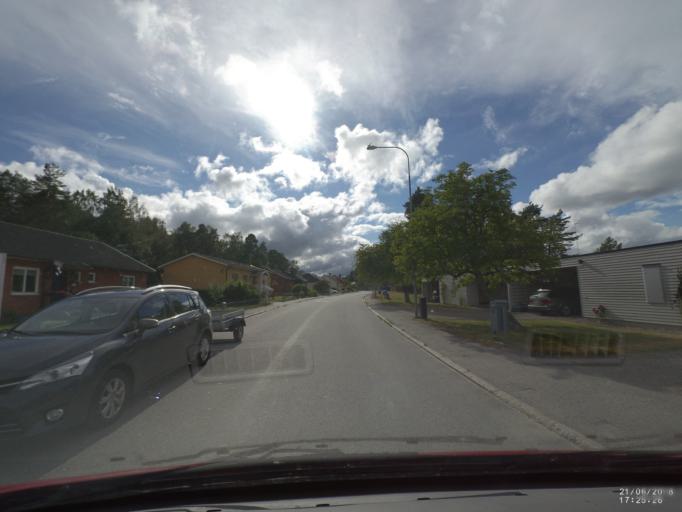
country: SE
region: Soedermanland
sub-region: Nykopings Kommun
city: Nykoping
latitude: 58.7509
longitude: 17.0509
